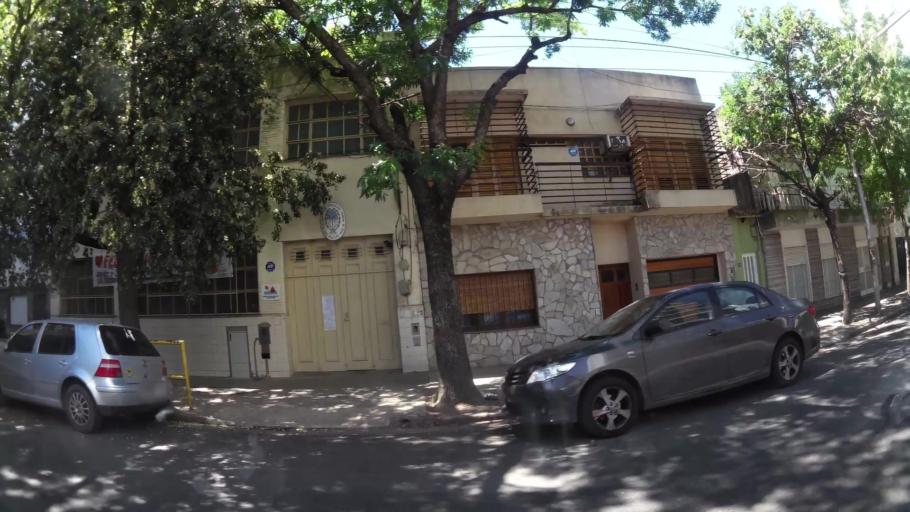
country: AR
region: Santa Fe
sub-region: Departamento de Rosario
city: Rosario
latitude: -32.9458
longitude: -60.6630
